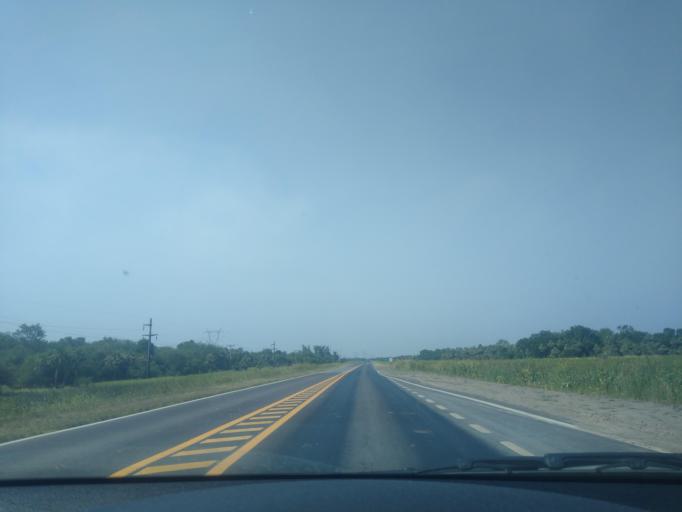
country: AR
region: Chaco
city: Fontana
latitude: -27.5737
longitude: -59.1561
